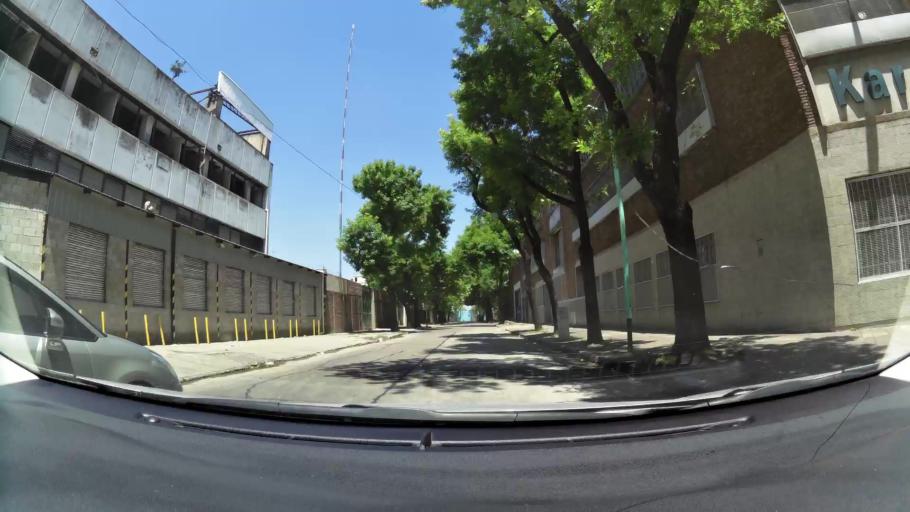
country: AR
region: Buenos Aires
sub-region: Partido de Avellaneda
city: Avellaneda
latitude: -34.6571
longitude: -58.3902
